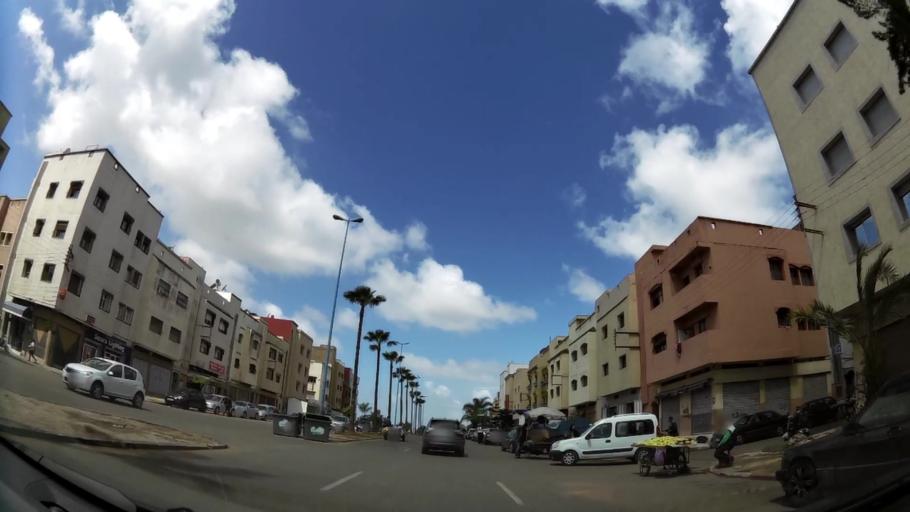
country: MA
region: Grand Casablanca
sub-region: Casablanca
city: Casablanca
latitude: 33.5390
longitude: -7.5925
